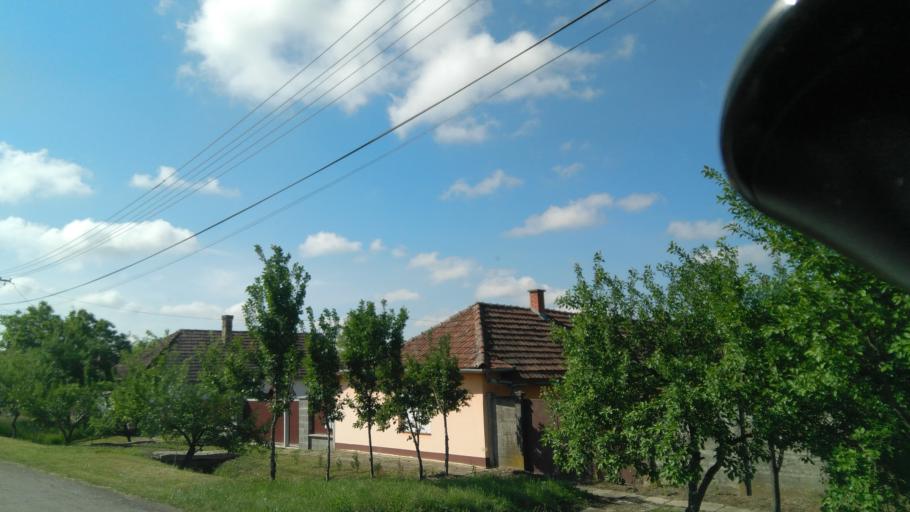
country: HU
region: Bekes
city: Bekes
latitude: 46.7855
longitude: 21.1204
